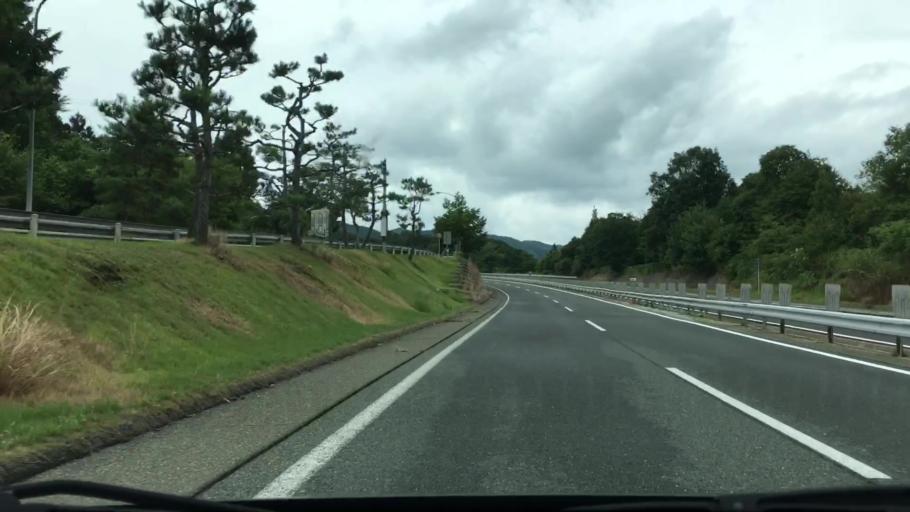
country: JP
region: Okayama
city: Niimi
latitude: 34.8930
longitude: 133.2562
